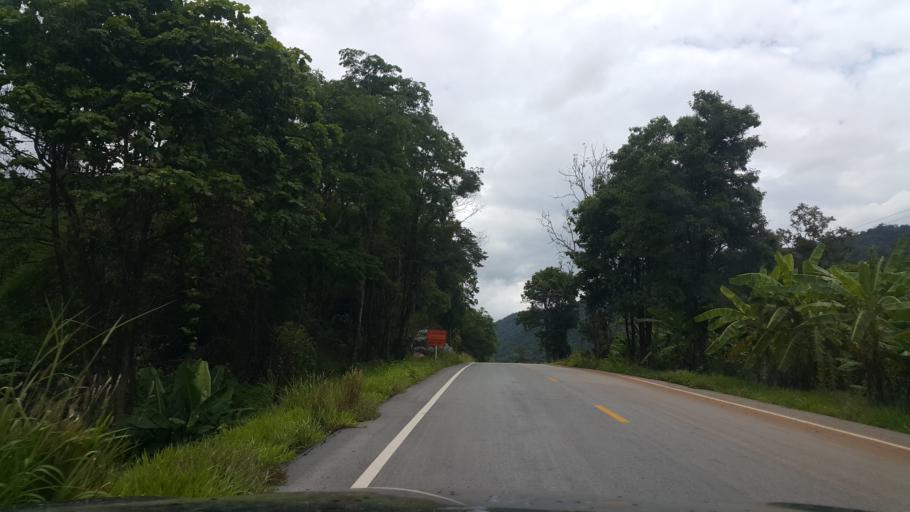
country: TH
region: Phitsanulok
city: Chat Trakan
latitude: 17.3538
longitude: 100.7279
